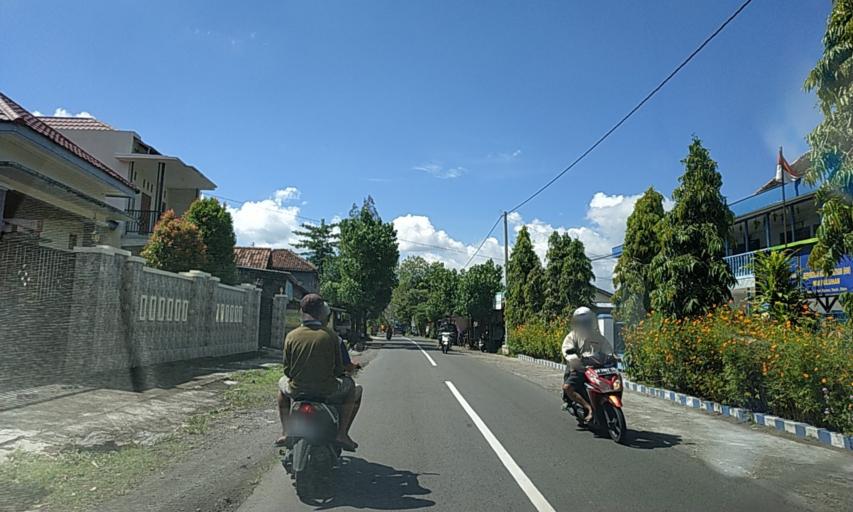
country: ID
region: Central Java
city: Trucuk
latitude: -7.7262
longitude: 110.6752
